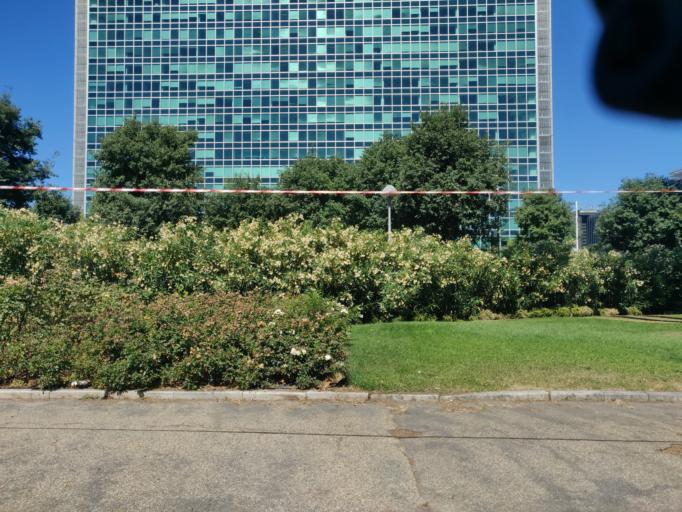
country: IT
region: Latium
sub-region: Citta metropolitana di Roma Capitale
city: Selcetta
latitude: 41.8269
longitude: 12.4728
